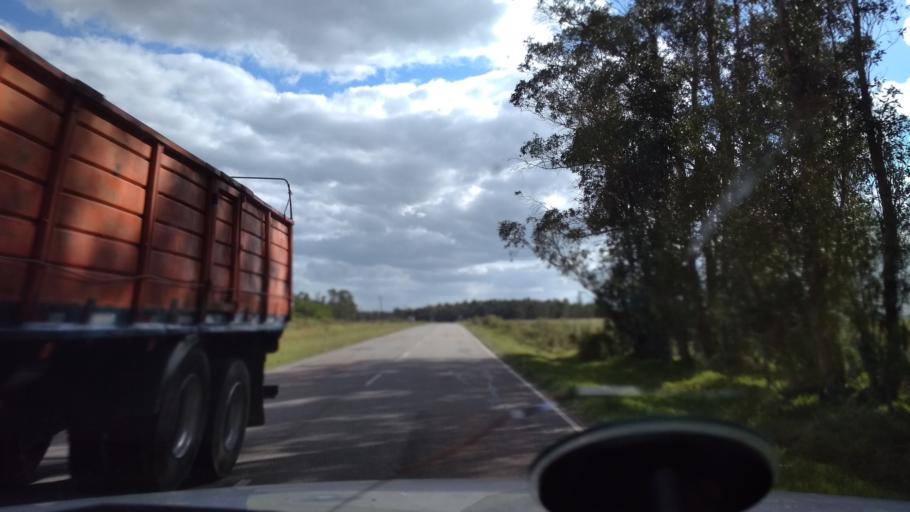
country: UY
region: Florida
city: Casupa
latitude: -34.1644
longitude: -55.7087
